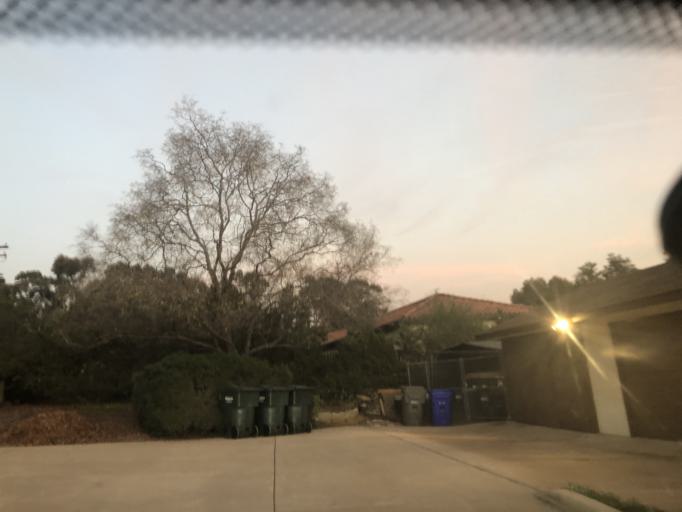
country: US
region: California
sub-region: San Diego County
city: Bonita
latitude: 32.6601
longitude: -117.0456
